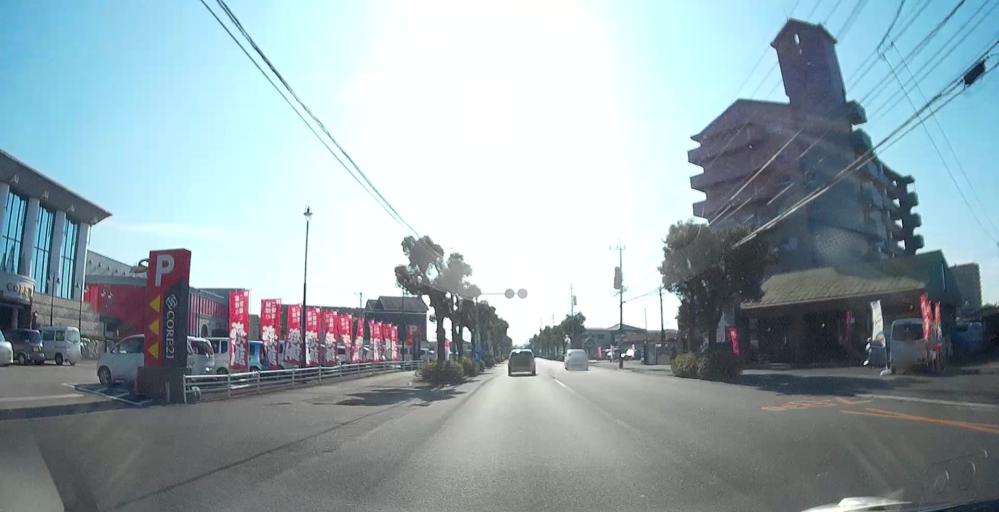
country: JP
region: Kumamoto
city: Kumamoto
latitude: 32.7508
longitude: 130.6857
